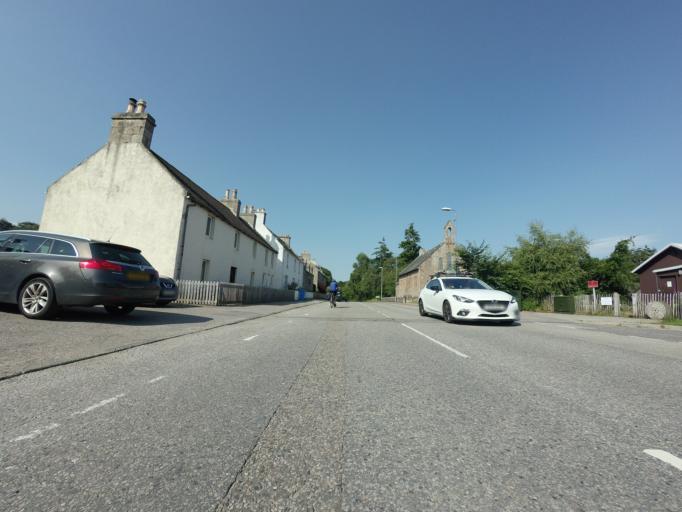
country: GB
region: Scotland
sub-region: Highland
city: Evanton
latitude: 57.6636
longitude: -4.3364
